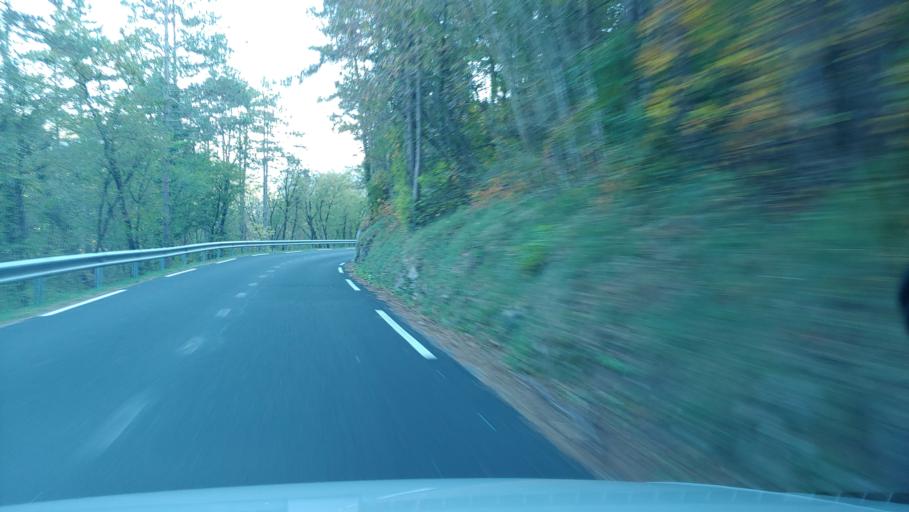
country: SI
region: Ajdovscina
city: Ajdovscina
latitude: 45.8106
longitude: 13.8563
